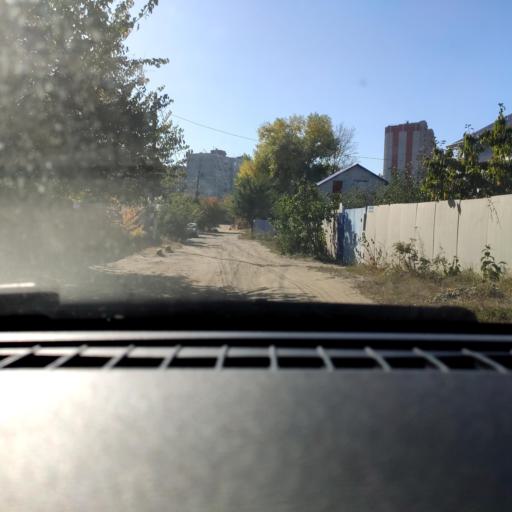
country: RU
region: Voronezj
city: Voronezh
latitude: 51.6646
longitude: 39.2861
